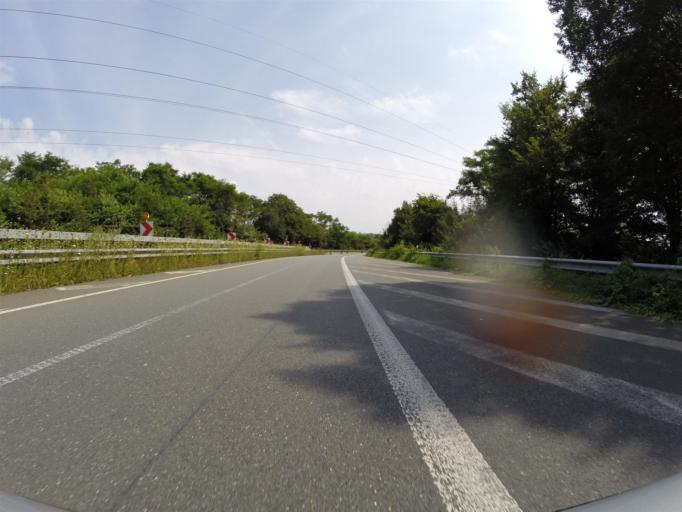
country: DE
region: North Rhine-Westphalia
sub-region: Regierungsbezirk Detmold
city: Herford
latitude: 52.1320
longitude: 8.6629
